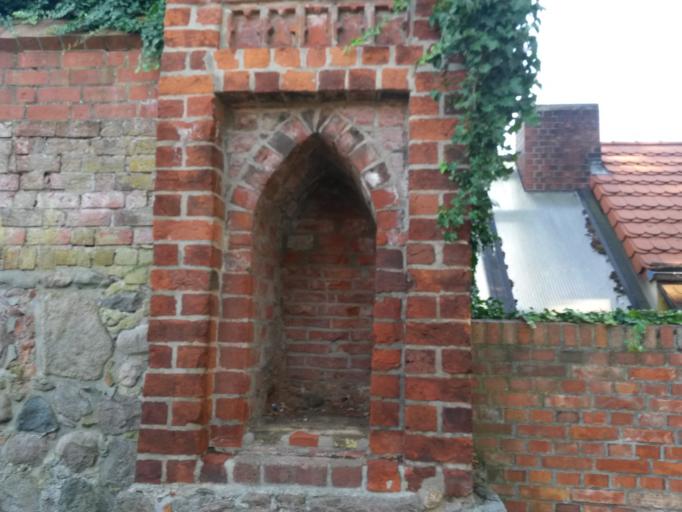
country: DE
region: Brandenburg
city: Angermunde
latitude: 53.0158
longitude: 14.0068
